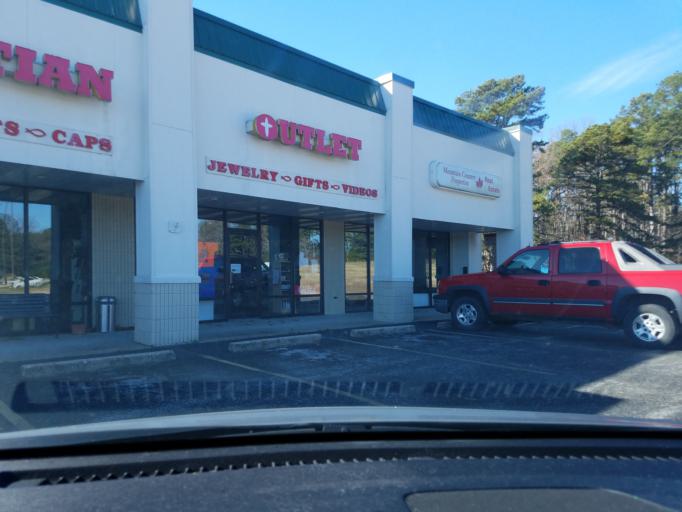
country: US
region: Arkansas
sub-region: Carroll County
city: Eureka Springs
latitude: 36.3927
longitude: -93.7104
